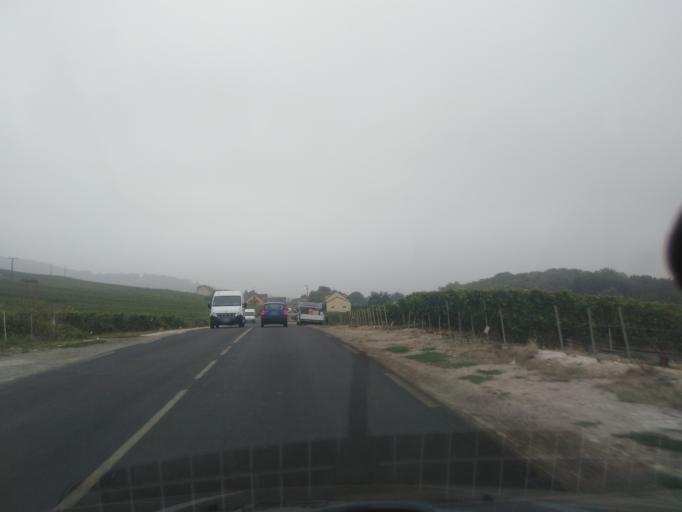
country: FR
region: Champagne-Ardenne
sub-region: Departement de la Marne
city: Mardeuil
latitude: 49.0700
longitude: 3.9157
